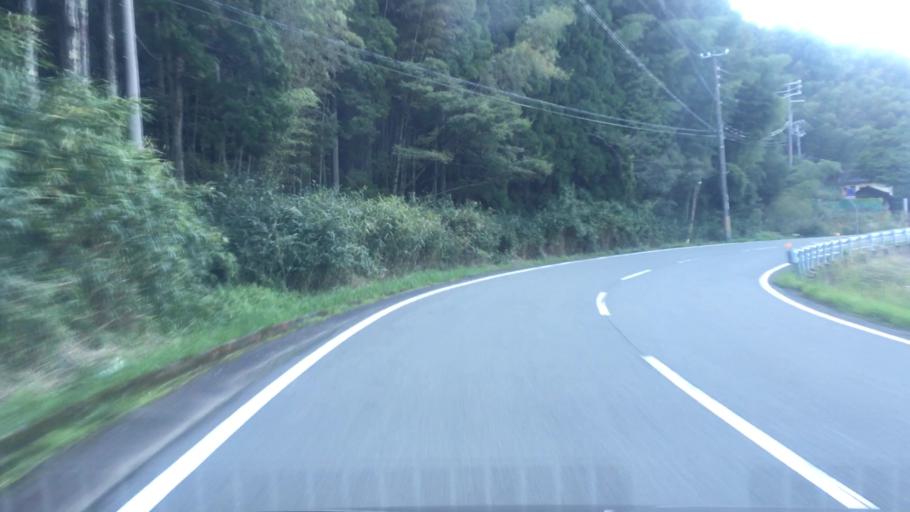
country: JP
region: Hyogo
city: Toyooka
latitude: 35.6162
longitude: 134.8243
